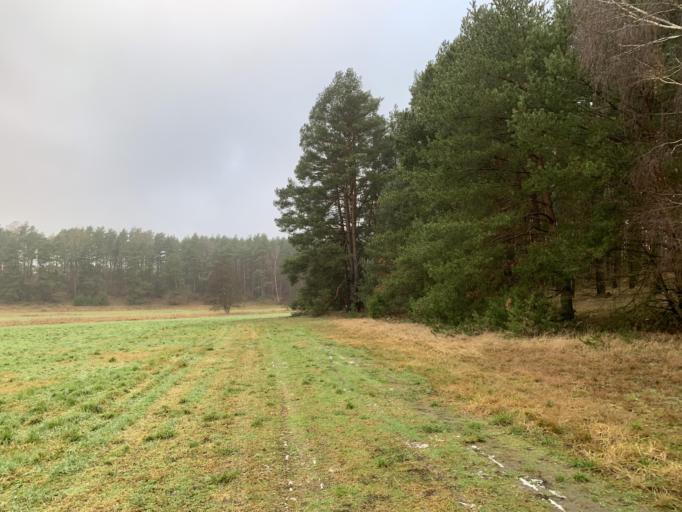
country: DE
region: Mecklenburg-Vorpommern
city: Blankensee
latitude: 53.4033
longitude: 13.2754
